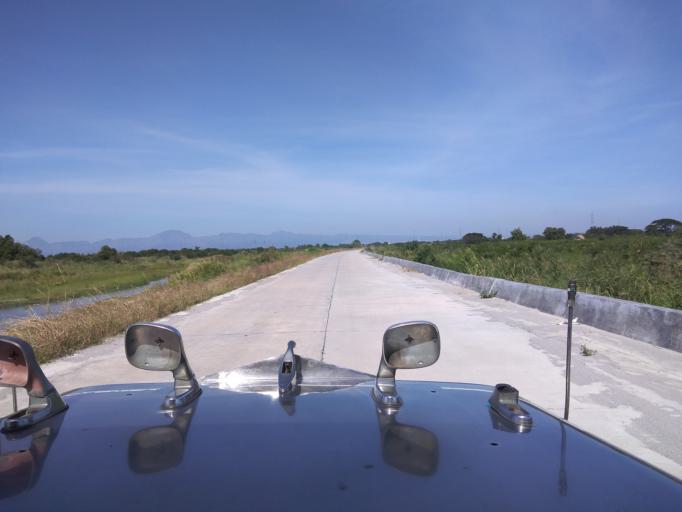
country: PH
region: Central Luzon
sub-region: Province of Pampanga
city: Bacolor
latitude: 14.9953
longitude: 120.6676
